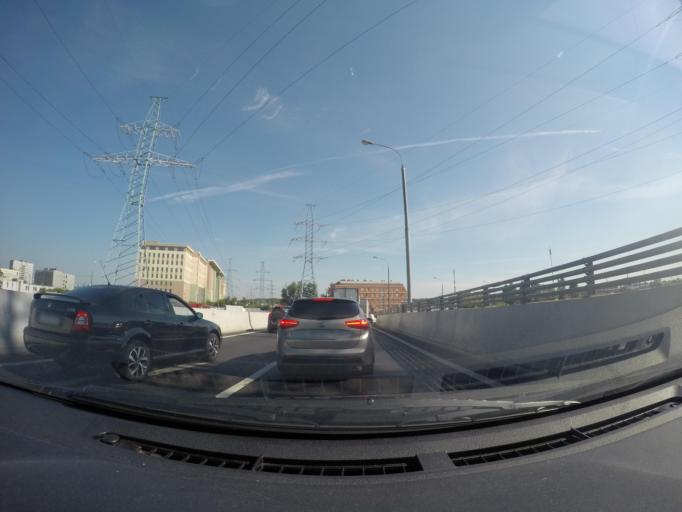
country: RU
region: Moscow
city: Veshnyaki
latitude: 55.7125
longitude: 37.8340
